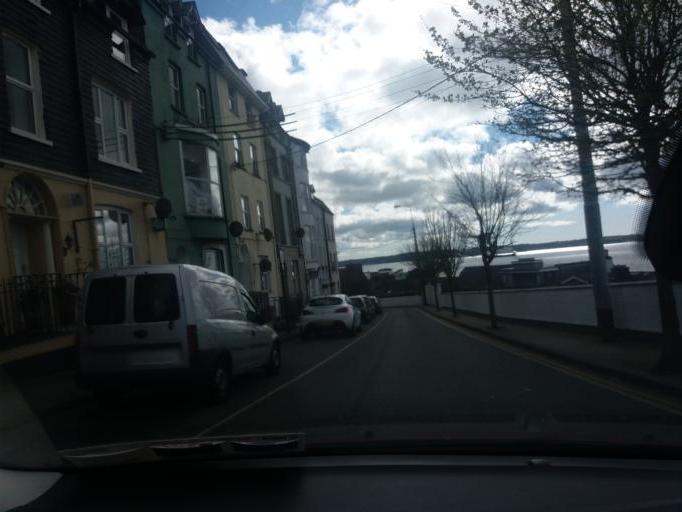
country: IE
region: Munster
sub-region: County Cork
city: Cobh
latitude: 51.8509
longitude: -8.2919
